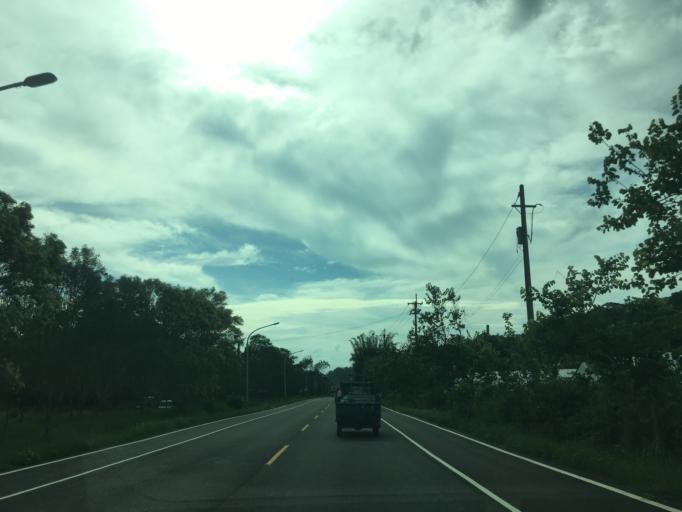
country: TW
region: Taiwan
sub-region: Chiayi
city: Jiayi Shi
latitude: 23.4496
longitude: 120.5727
